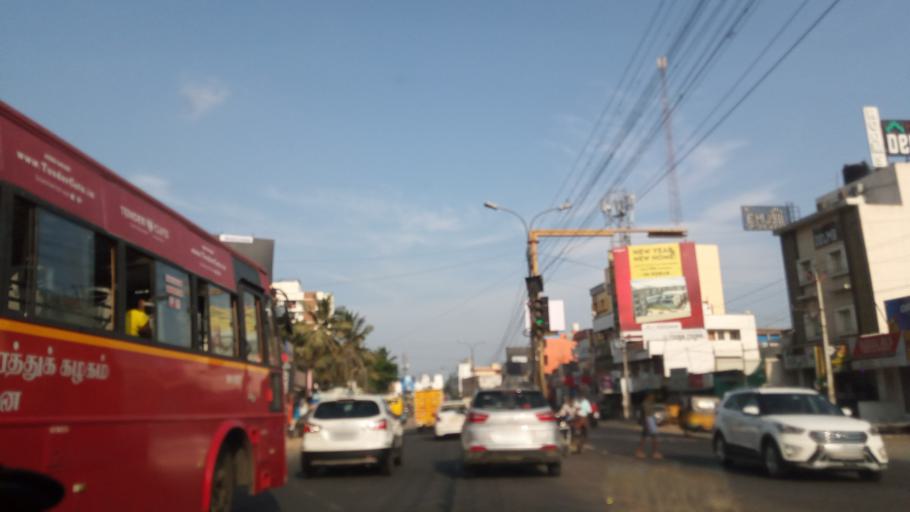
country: IN
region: Tamil Nadu
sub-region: Thiruvallur
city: Porur
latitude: 13.0381
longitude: 80.1354
